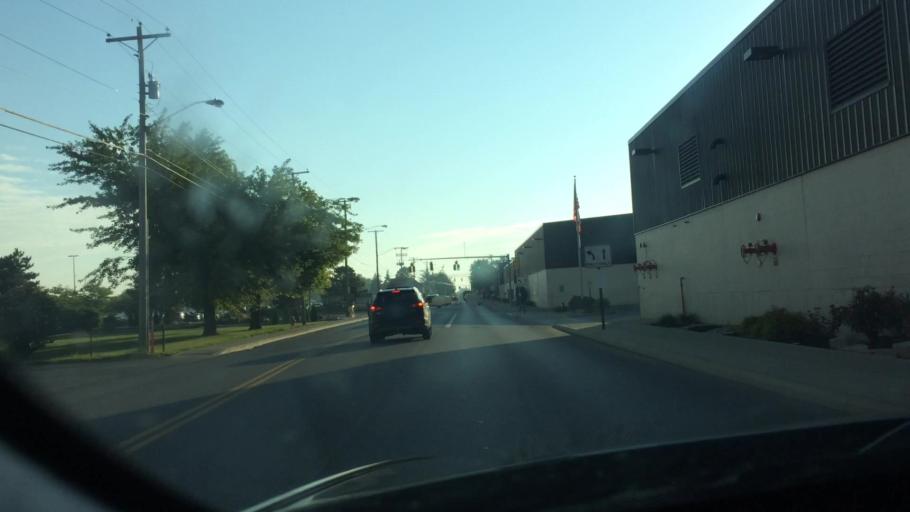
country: US
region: Ohio
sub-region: Hancock County
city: Findlay
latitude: 41.0256
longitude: -83.6630
